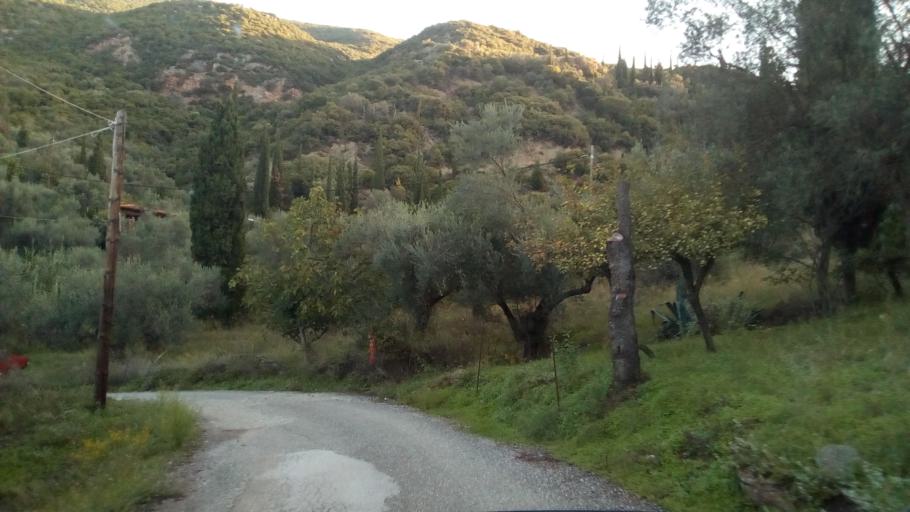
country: GR
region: West Greece
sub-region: Nomos Aitolias kai Akarnanias
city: Nafpaktos
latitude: 38.4079
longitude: 21.8001
